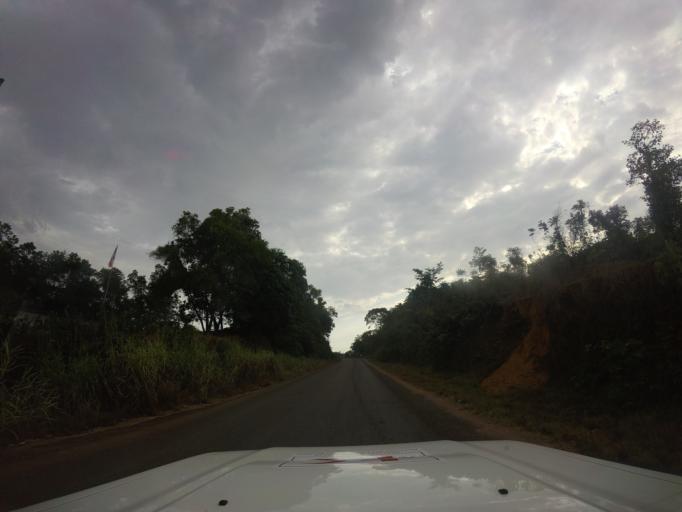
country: LR
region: Grand Cape Mount
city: Robertsport
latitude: 6.8115
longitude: -11.1402
